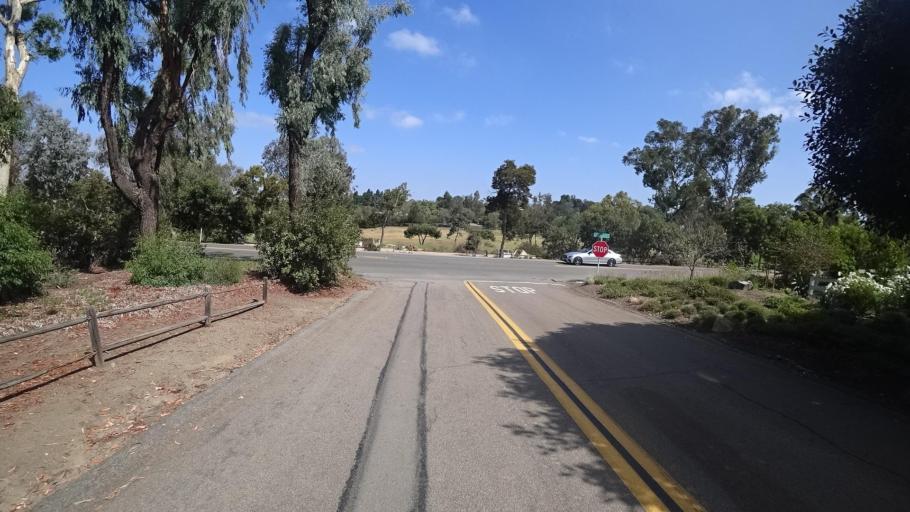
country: US
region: California
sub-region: San Diego County
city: Rancho Santa Fe
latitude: 33.0228
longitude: -117.2134
